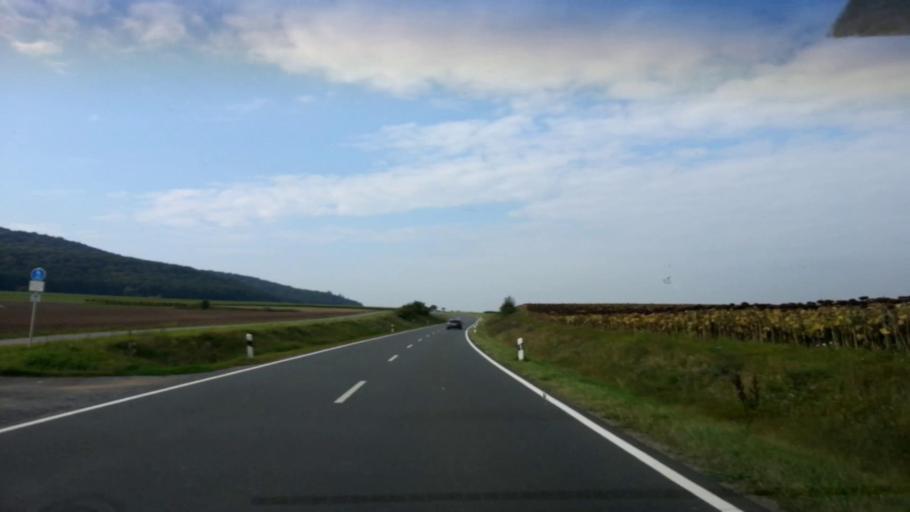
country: DE
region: Bavaria
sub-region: Regierungsbezirk Unterfranken
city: Wiesenbronn
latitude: 49.7387
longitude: 10.2914
